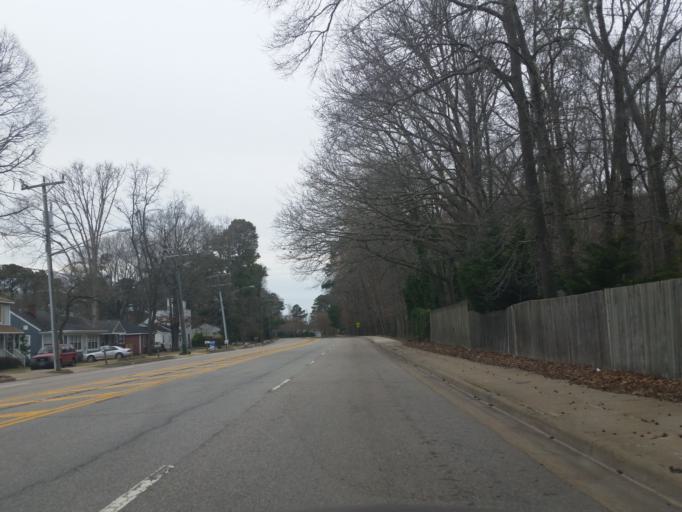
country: US
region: Virginia
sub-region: City of Virginia Beach
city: Virginia Beach
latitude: 36.8263
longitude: -75.9761
